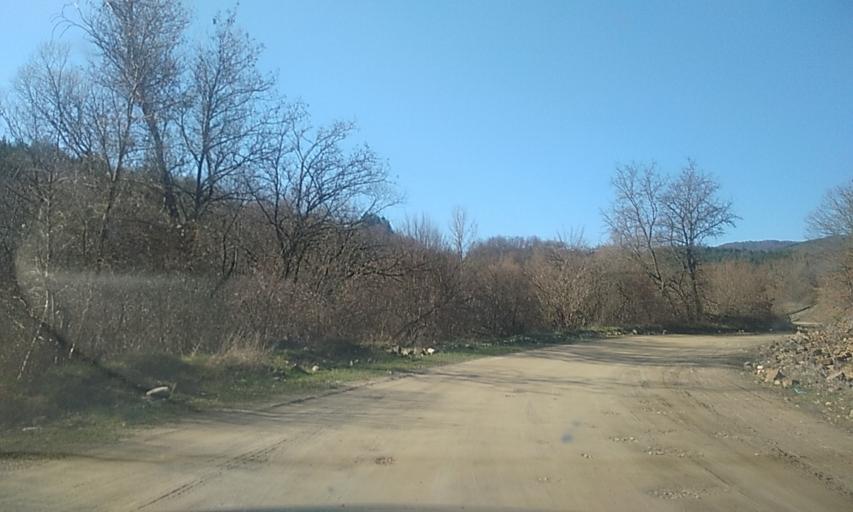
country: RS
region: Central Serbia
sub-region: Pcinjski Okrug
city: Bosilegrad
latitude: 42.3648
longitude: 22.4320
